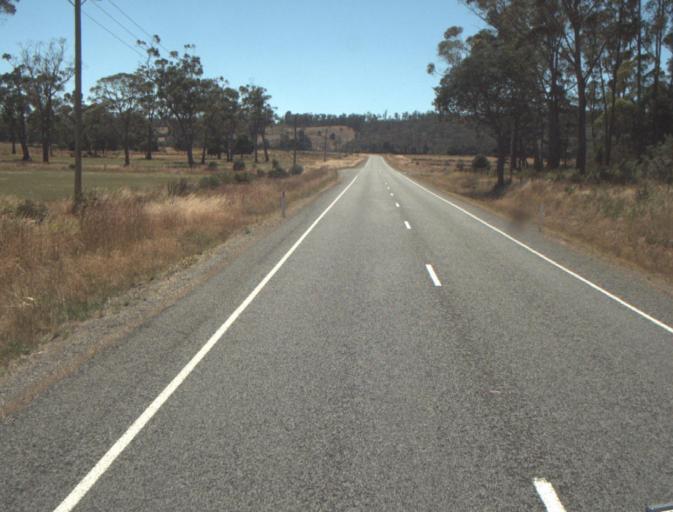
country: AU
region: Tasmania
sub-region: Launceston
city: Newstead
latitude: -41.3652
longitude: 147.3315
